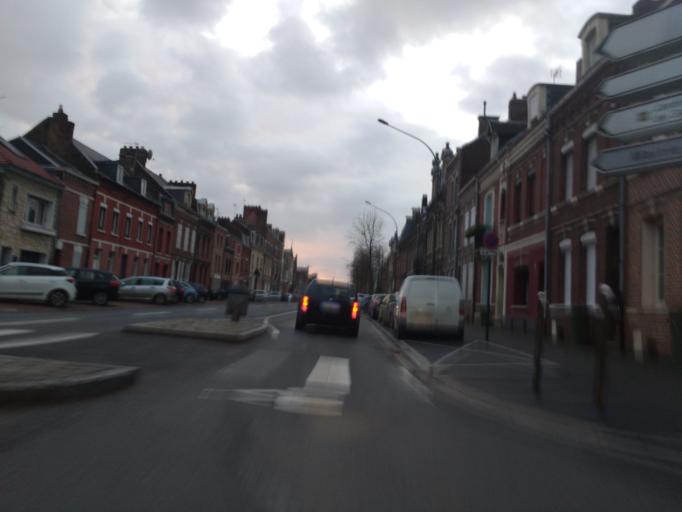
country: FR
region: Picardie
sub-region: Departement de la Somme
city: Rivery
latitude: 49.8847
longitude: 2.3217
